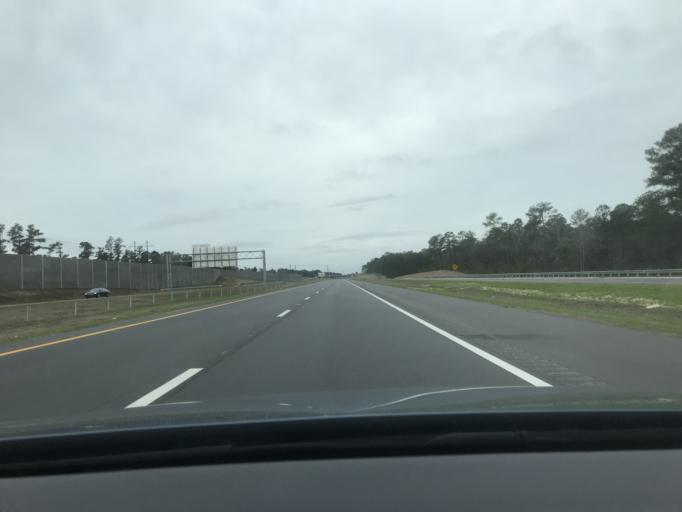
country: US
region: North Carolina
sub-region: Cumberland County
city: Fort Bragg
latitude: 35.1099
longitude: -78.9835
